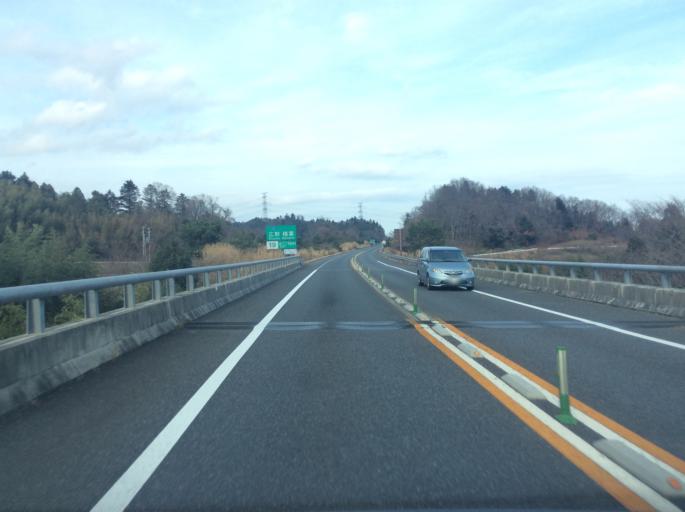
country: JP
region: Fukushima
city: Iwaki
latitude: 37.2258
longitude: 140.9772
